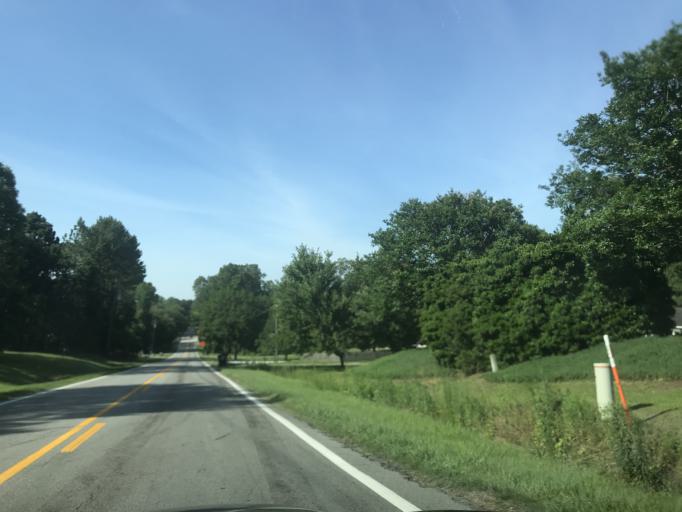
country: US
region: North Carolina
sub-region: Johnston County
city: Clayton
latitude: 35.5970
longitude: -78.5365
